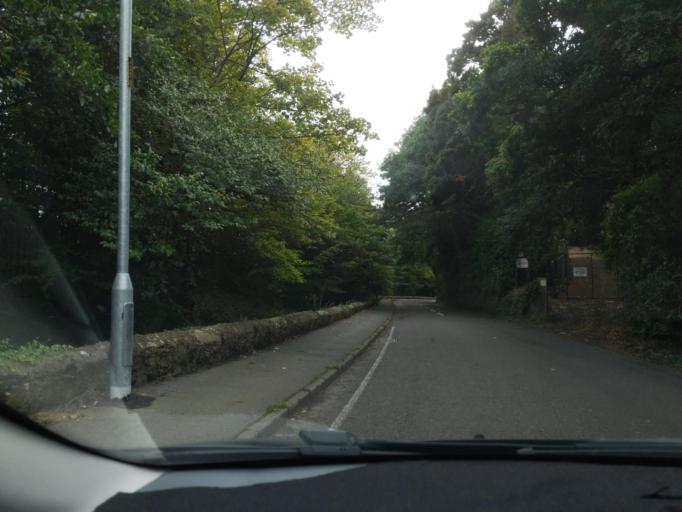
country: GB
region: England
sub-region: Cornwall
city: Par
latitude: 50.3541
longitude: -4.7111
